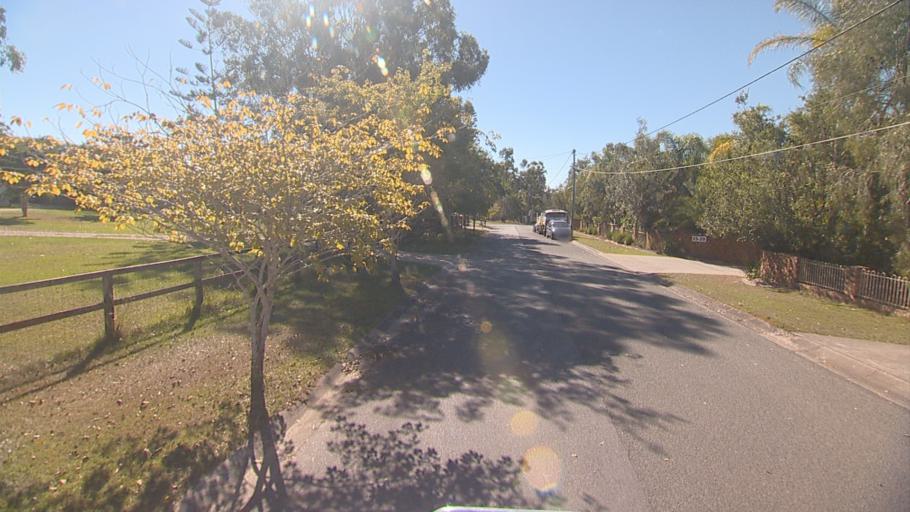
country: AU
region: Queensland
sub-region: Logan
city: Logan Reserve
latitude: -27.7037
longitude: 153.0706
